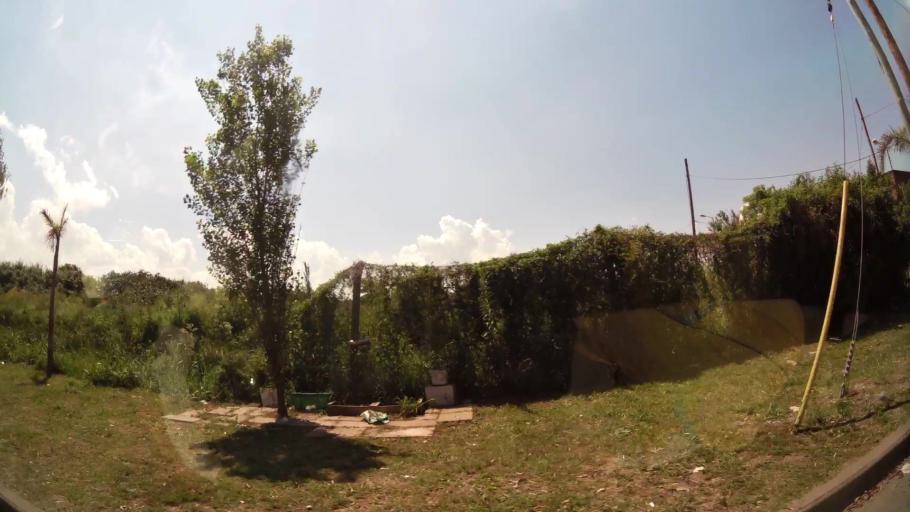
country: AR
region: Buenos Aires
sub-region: Partido de Tigre
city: Tigre
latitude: -34.4645
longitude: -58.5847
